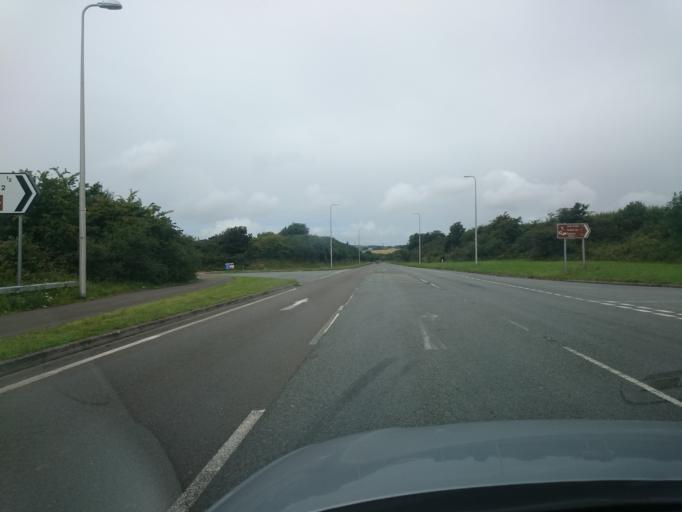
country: GB
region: Wales
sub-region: Pembrokeshire
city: Burton
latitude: 51.7104
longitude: -4.9357
